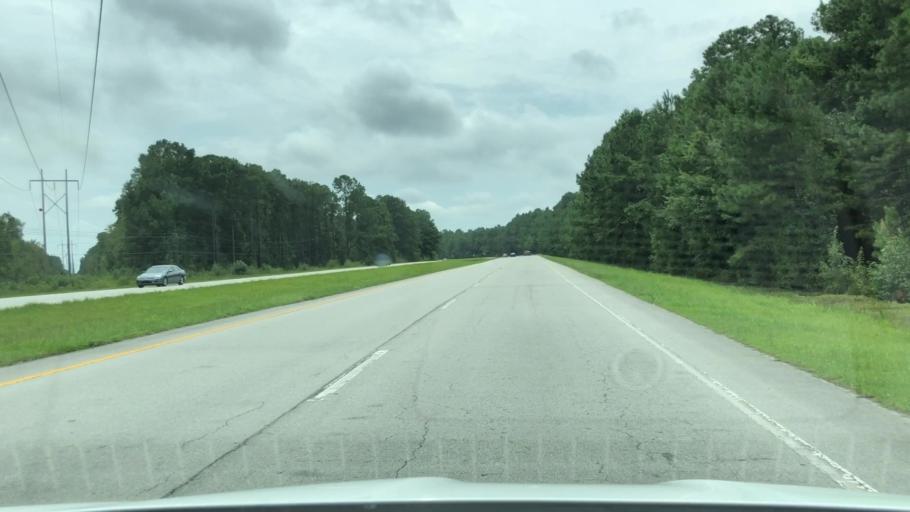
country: US
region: North Carolina
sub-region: Craven County
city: Havelock
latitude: 34.8409
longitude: -76.8824
